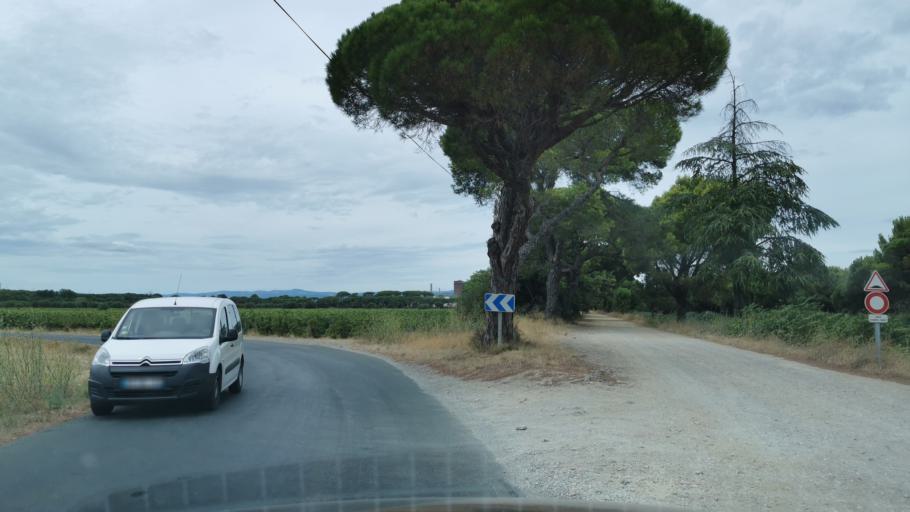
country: FR
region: Languedoc-Roussillon
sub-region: Departement de l'Aude
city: Saint-Marcel-sur-Aude
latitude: 43.2781
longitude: 2.9275
